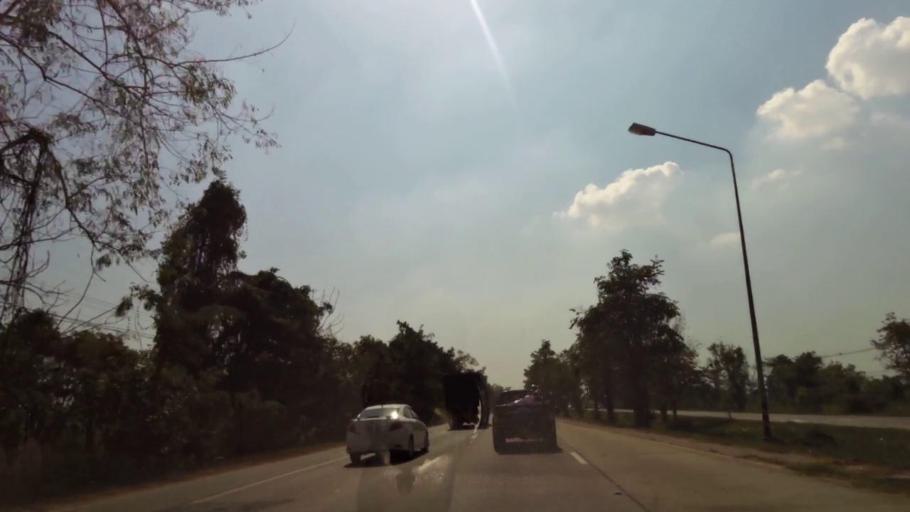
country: TH
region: Phichit
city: Wachira Barami
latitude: 16.5465
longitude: 100.1459
